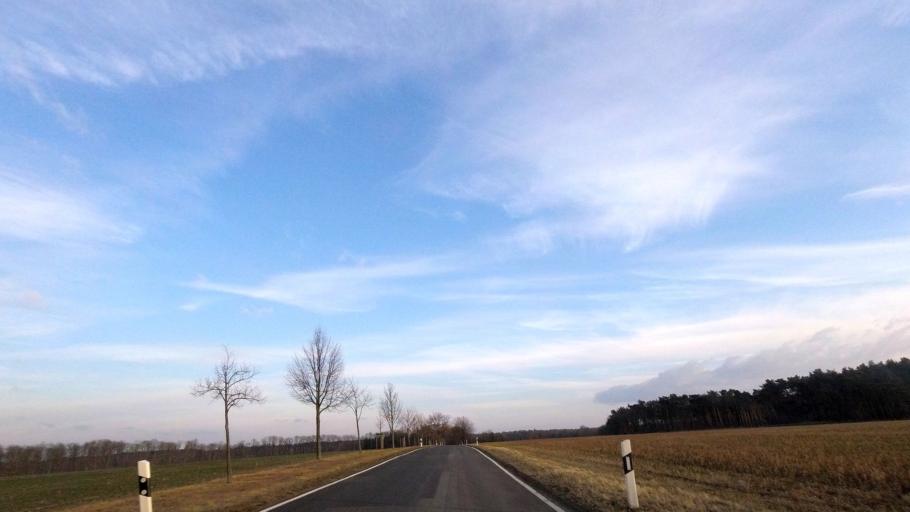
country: DE
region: Brandenburg
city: Niemegk
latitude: 52.0788
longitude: 12.6487
